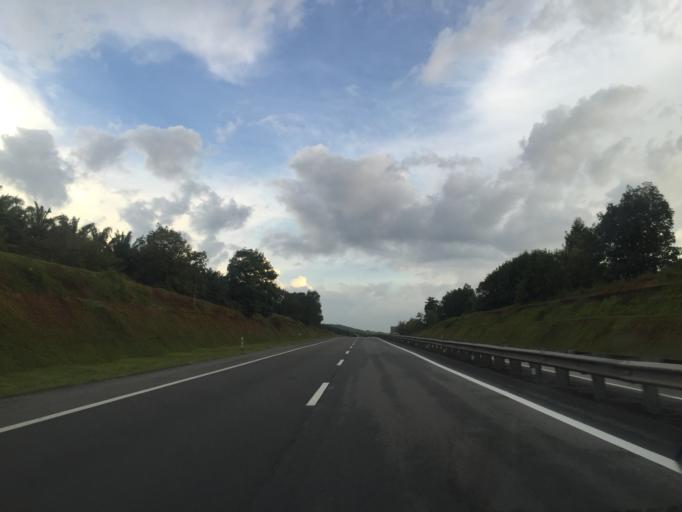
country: MY
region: Kedah
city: Gurun
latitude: 5.7957
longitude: 100.4978
